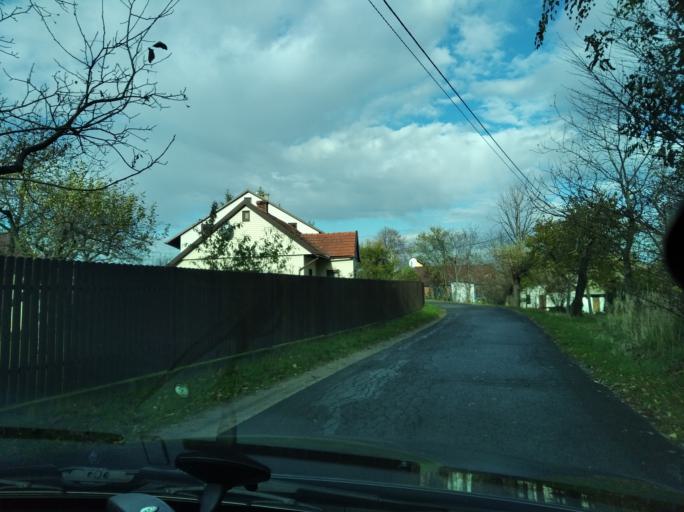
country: PL
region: Subcarpathian Voivodeship
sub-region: Powiat debicki
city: Debica
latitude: 50.0340
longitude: 21.4527
